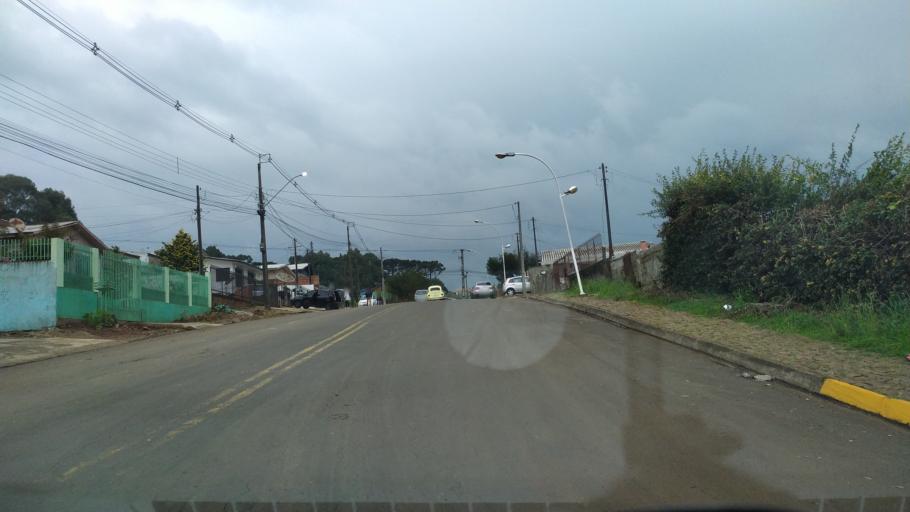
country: BR
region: Parana
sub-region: Palmas
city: Palmas
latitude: -26.4916
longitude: -51.9988
